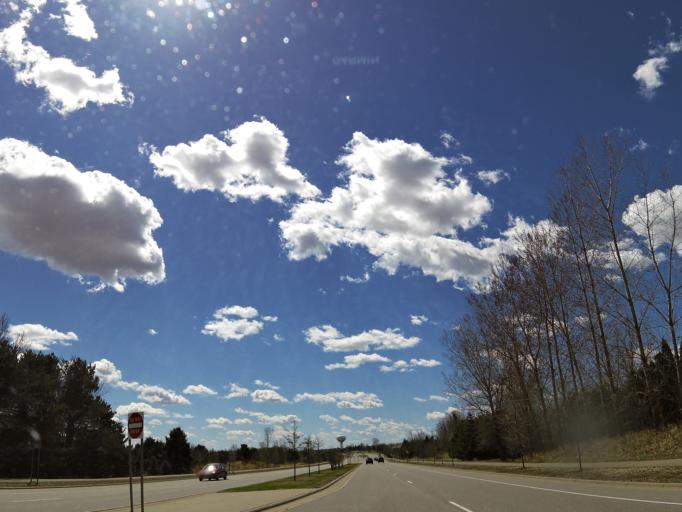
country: US
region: Minnesota
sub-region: Washington County
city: Woodbury
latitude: 44.9110
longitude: -92.9388
